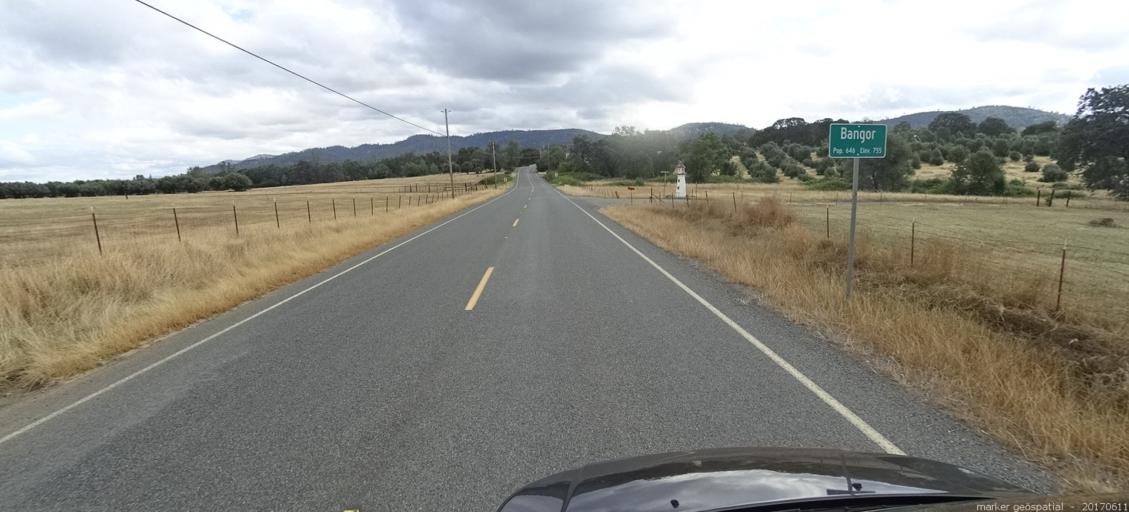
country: US
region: California
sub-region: Yuba County
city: Loma Rica
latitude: 39.3836
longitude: -121.4096
